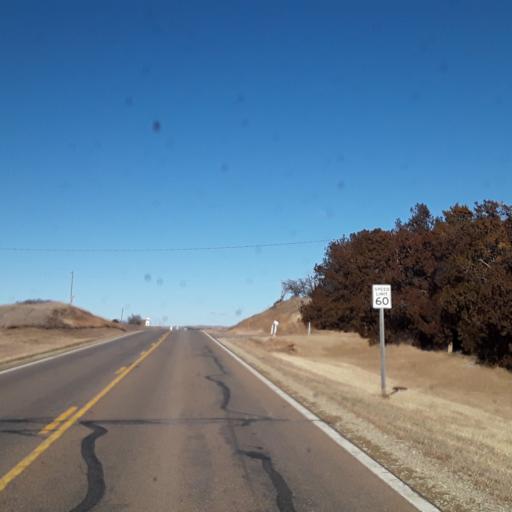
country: US
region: Kansas
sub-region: Lincoln County
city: Lincoln
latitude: 38.9885
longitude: -98.1512
